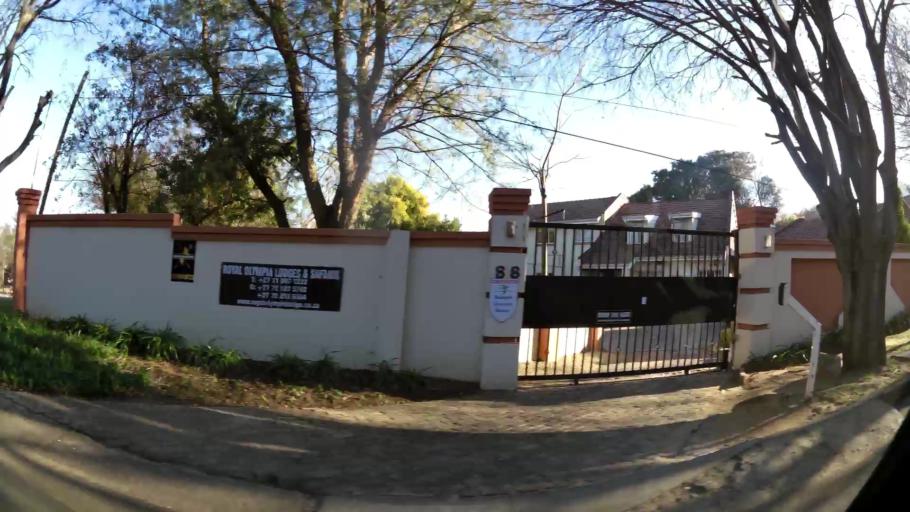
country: ZA
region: Gauteng
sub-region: City of Johannesburg Metropolitan Municipality
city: Midrand
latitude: -26.0358
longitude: 28.0724
